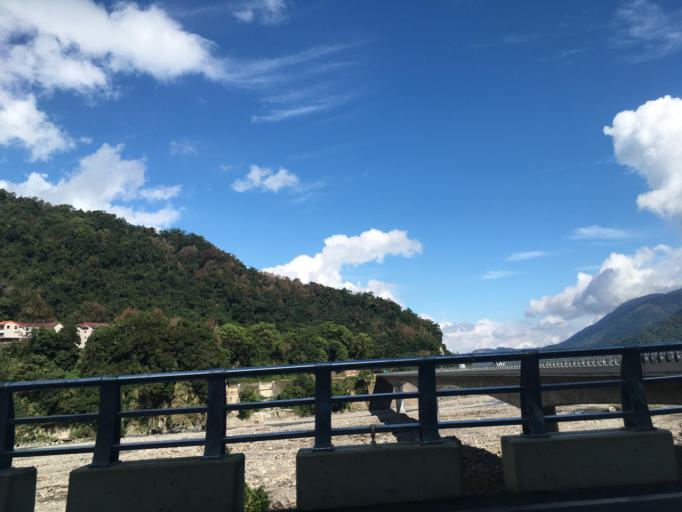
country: TW
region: Taiwan
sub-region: Yilan
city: Yilan
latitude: 24.5772
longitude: 121.4914
